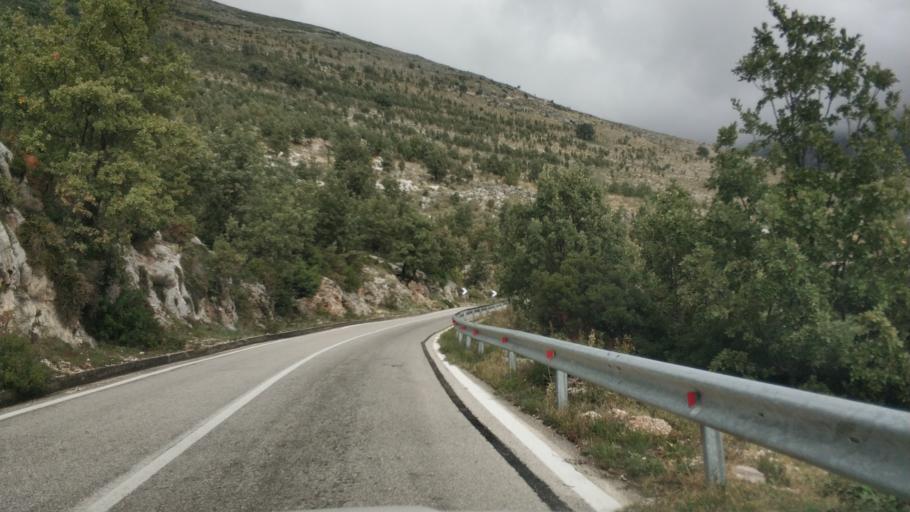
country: AL
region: Vlore
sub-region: Rrethi i Vlores
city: Vranisht
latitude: 40.1843
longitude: 19.6063
